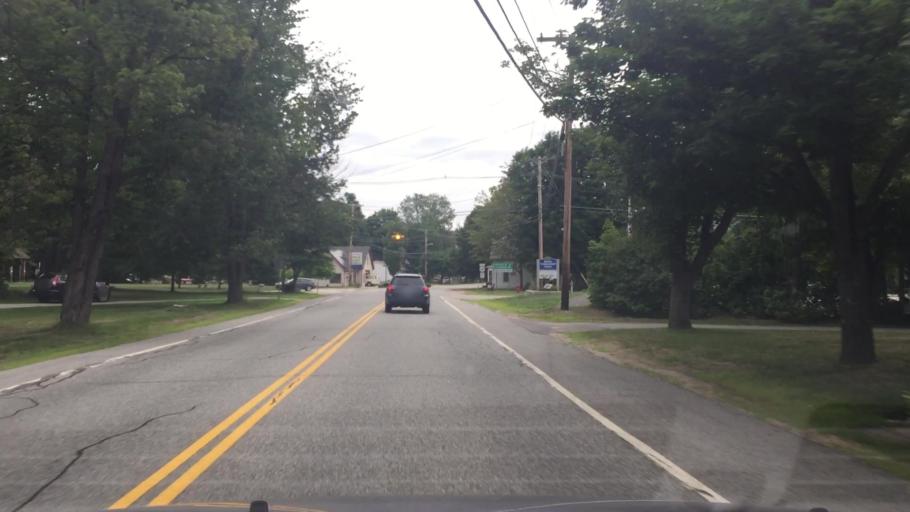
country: US
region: New Hampshire
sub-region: Carroll County
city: North Conway
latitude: 44.0779
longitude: -71.2831
